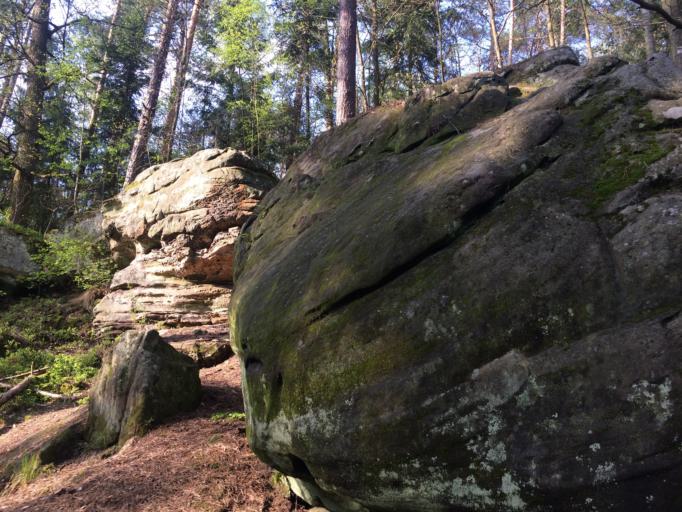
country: PL
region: Swietokrzyskie
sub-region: Powiat starachowicki
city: Brody
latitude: 51.0321
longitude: 21.1655
